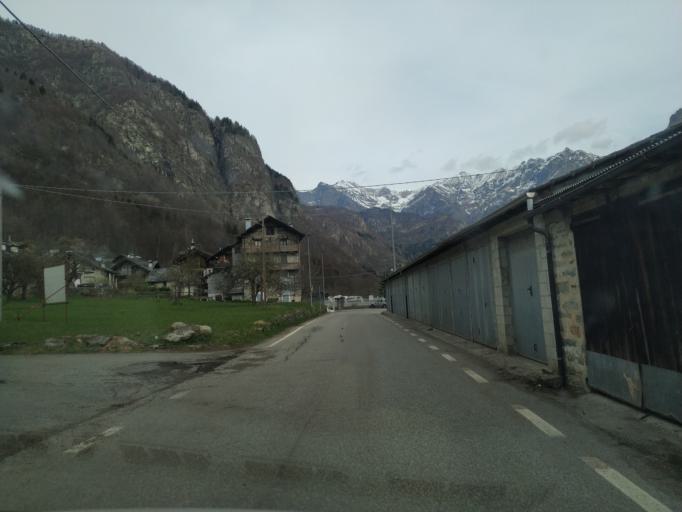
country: IT
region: Piedmont
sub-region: Provincia di Vercelli
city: Piode
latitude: 45.7794
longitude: 8.0420
